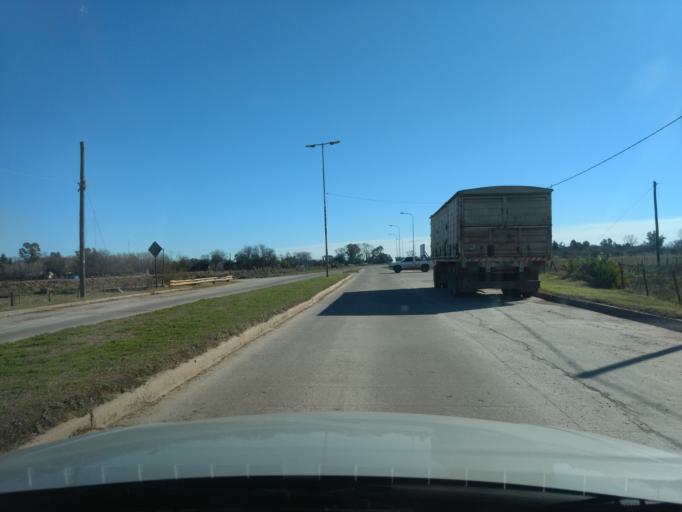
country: AR
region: Buenos Aires
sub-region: Partido de Navarro
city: Navarro
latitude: -34.9927
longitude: -59.2768
